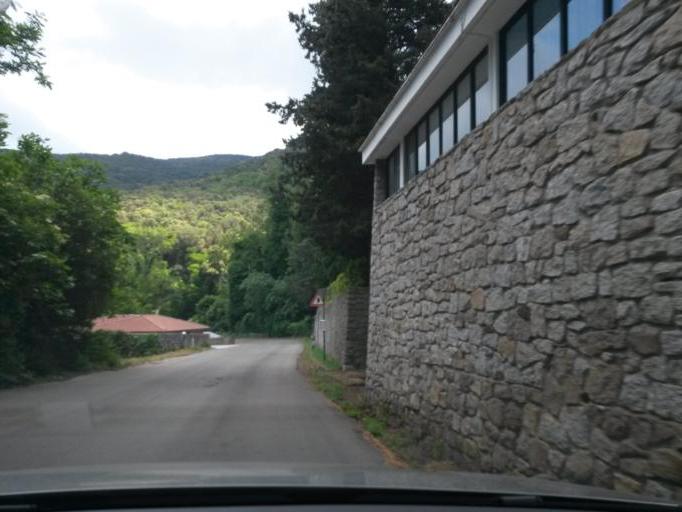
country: IT
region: Tuscany
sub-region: Provincia di Livorno
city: Marciana Marina
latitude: 42.7887
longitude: 10.1872
